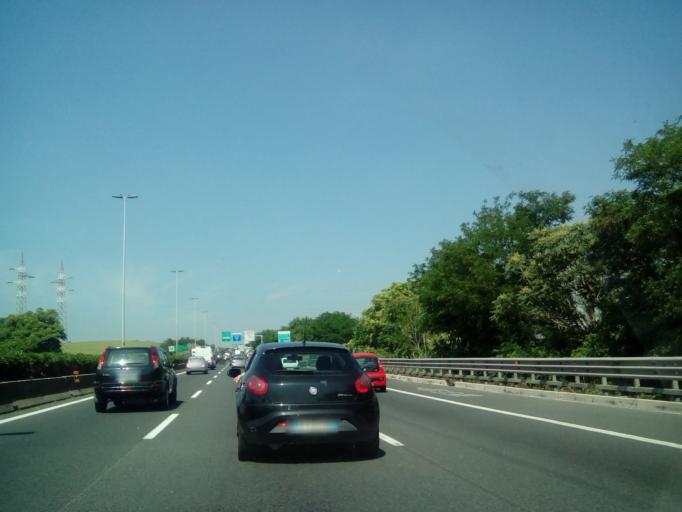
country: IT
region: Latium
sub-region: Citta metropolitana di Roma Capitale
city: Selcetta
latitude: 41.7995
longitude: 12.4646
